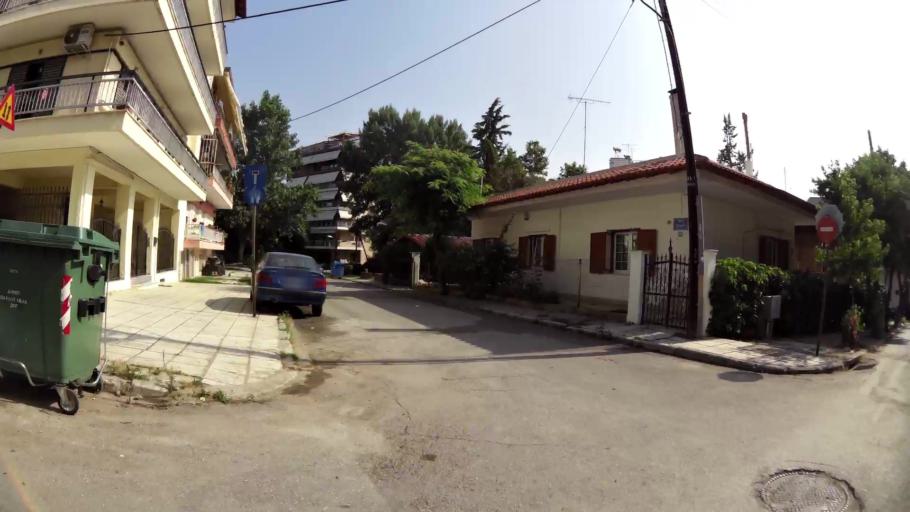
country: GR
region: Central Macedonia
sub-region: Nomos Thessalonikis
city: Stavroupoli
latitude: 40.6698
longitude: 22.9296
